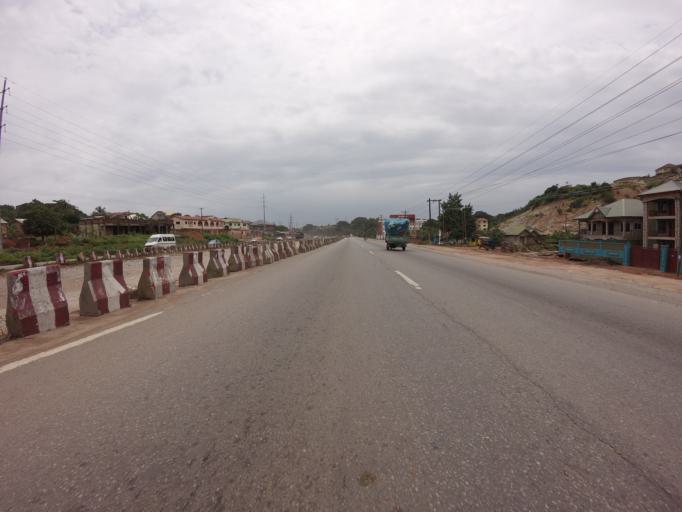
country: GH
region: Greater Accra
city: Dome
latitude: 5.6773
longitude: -0.2729
